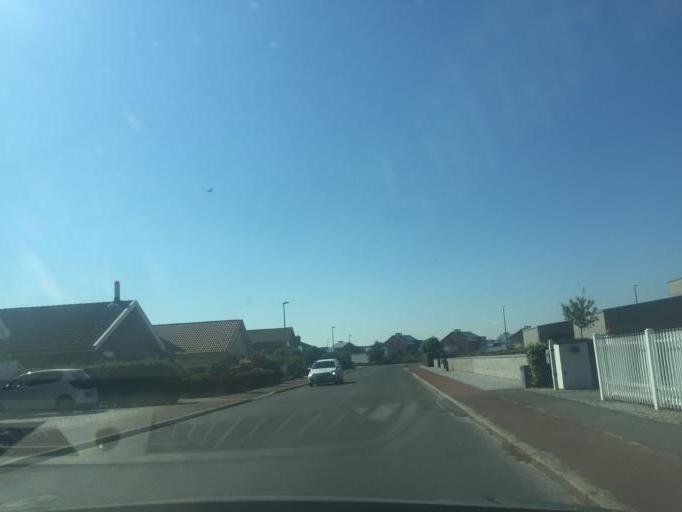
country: DK
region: Central Jutland
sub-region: Hedensted Kommune
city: Juelsminde
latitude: 55.7156
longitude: 10.0107
